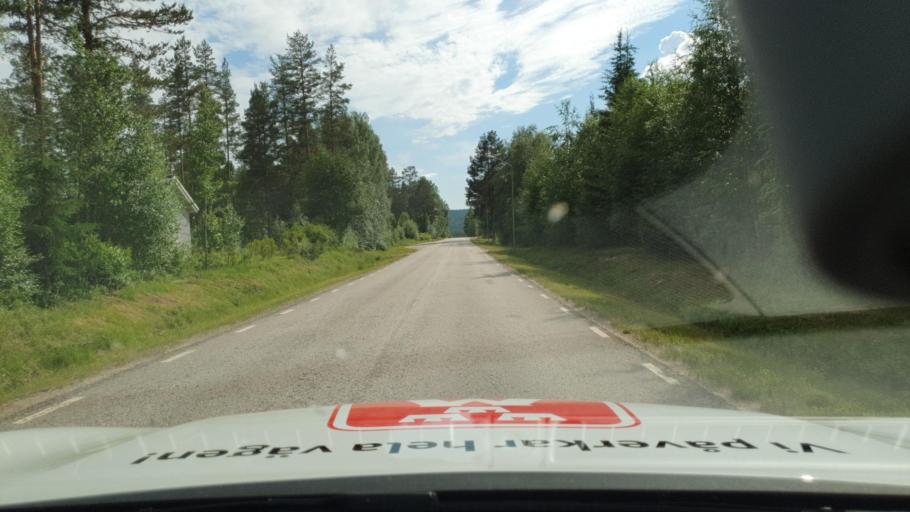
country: NO
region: Hedmark
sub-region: Trysil
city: Innbygda
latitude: 60.9651
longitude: 12.4821
